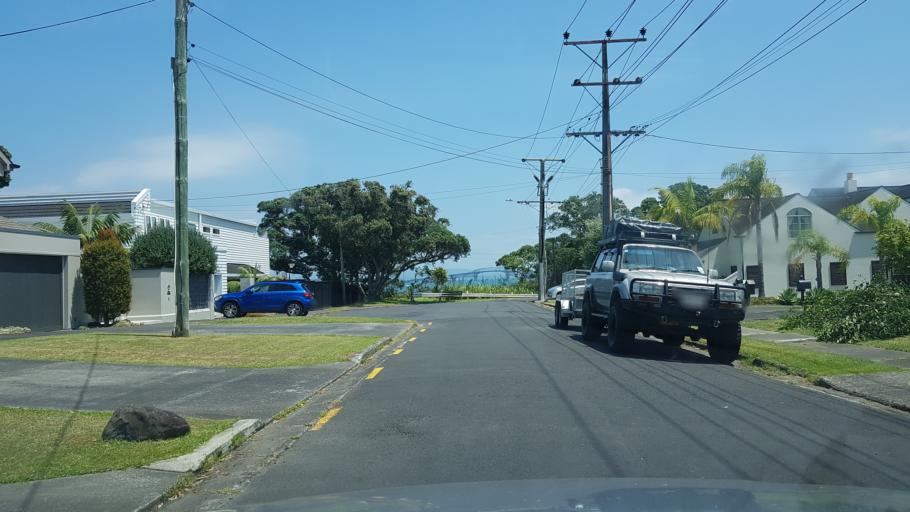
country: NZ
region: Auckland
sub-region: Auckland
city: North Shore
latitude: -36.8185
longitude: 174.7856
